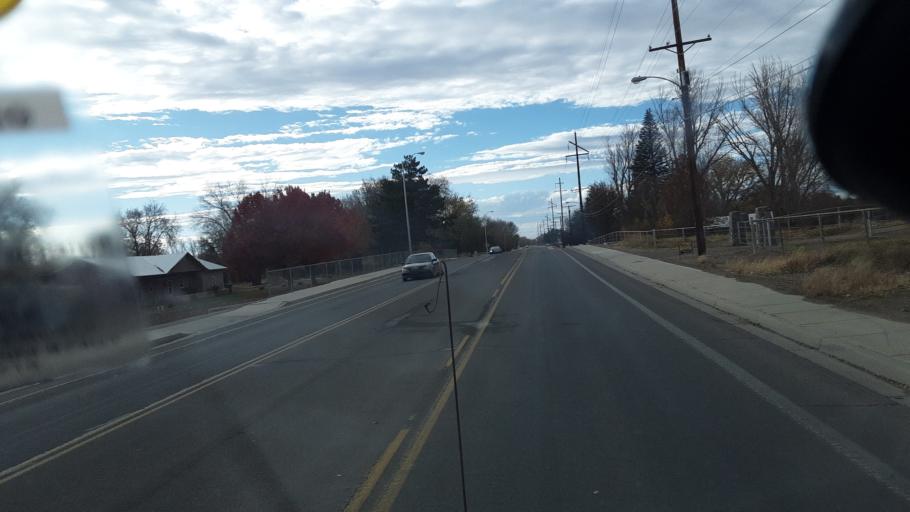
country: US
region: New Mexico
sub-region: San Juan County
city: Farmington
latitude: 36.7266
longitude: -108.1805
